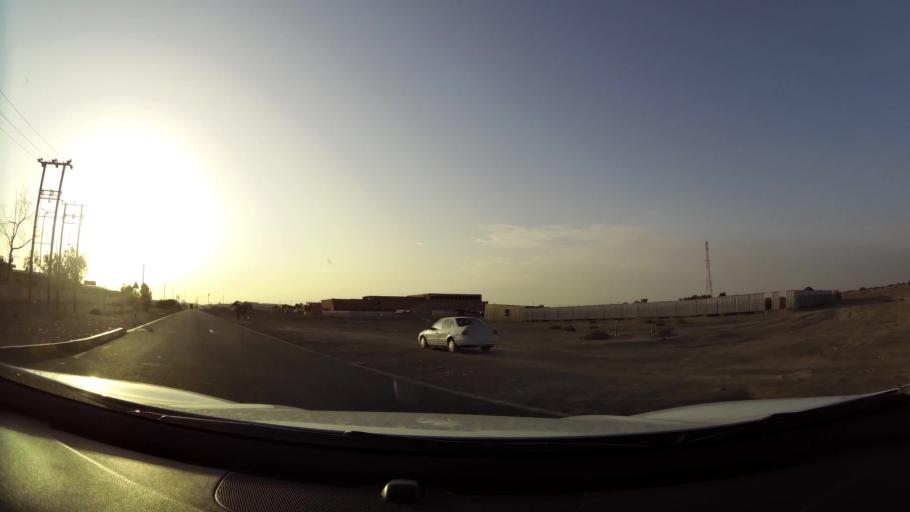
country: AE
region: Abu Dhabi
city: Al Ain
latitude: 24.1594
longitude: 55.8213
